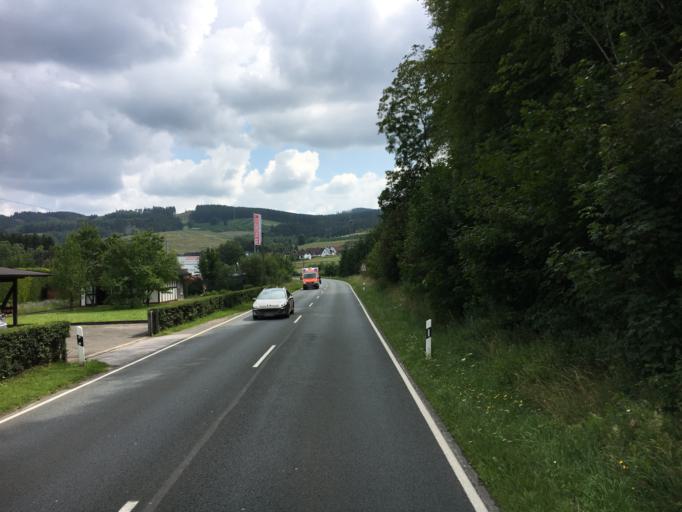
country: DE
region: North Rhine-Westphalia
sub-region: Regierungsbezirk Arnsberg
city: Lennestadt
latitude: 51.1250
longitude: 8.0383
